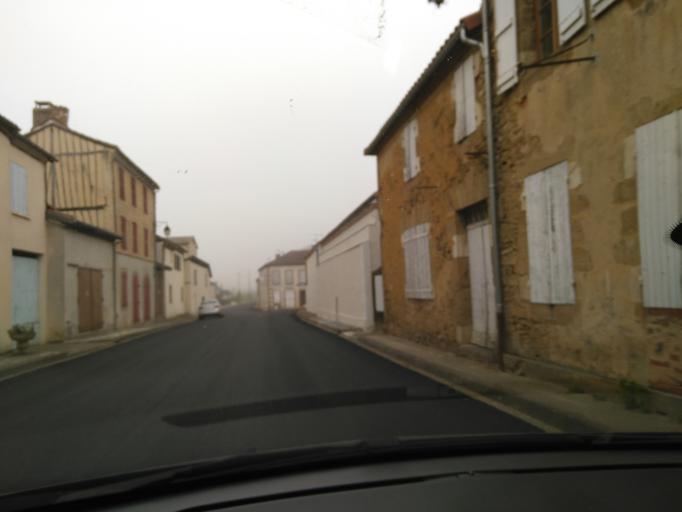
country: FR
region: Midi-Pyrenees
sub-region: Departement du Gers
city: Le Houga
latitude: 43.8552
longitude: -0.1817
